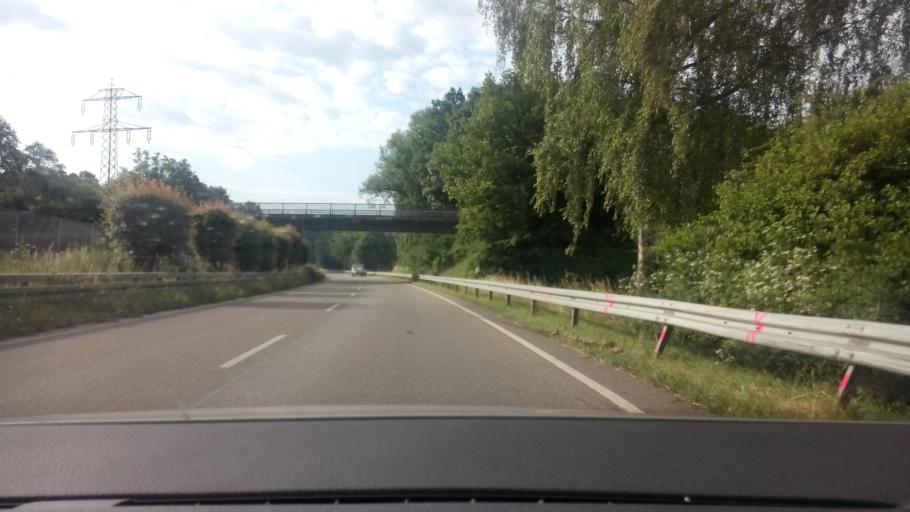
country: DE
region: Bavaria
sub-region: Upper Bavaria
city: Karlsfeld
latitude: 48.2323
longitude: 11.4534
